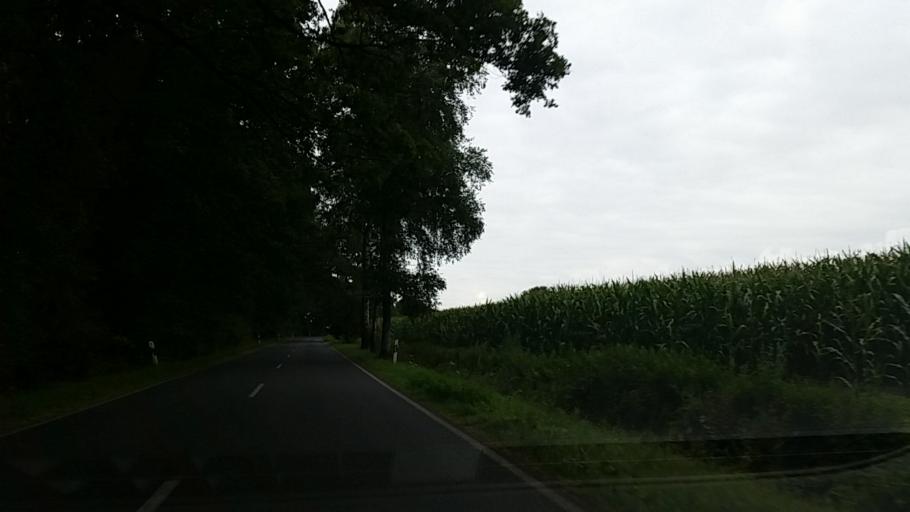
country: DE
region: Lower Saxony
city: Vollersode
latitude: 53.4021
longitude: 8.9221
